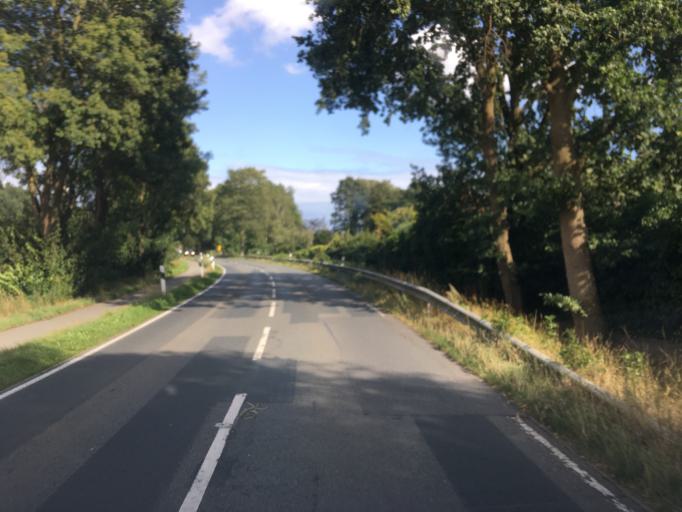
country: DE
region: Lower Saxony
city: Wardenburg
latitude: 53.0674
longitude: 8.1786
